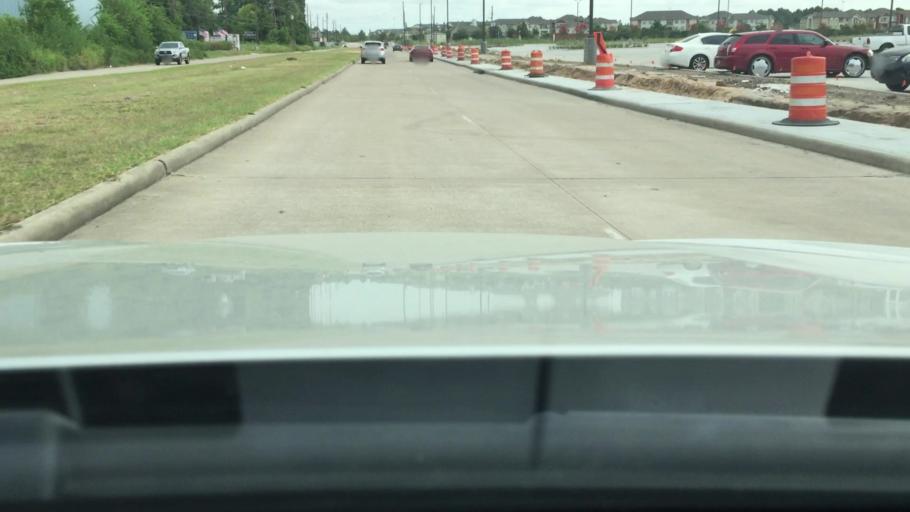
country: US
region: Texas
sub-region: Harris County
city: Jersey Village
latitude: 29.9439
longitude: -95.5467
